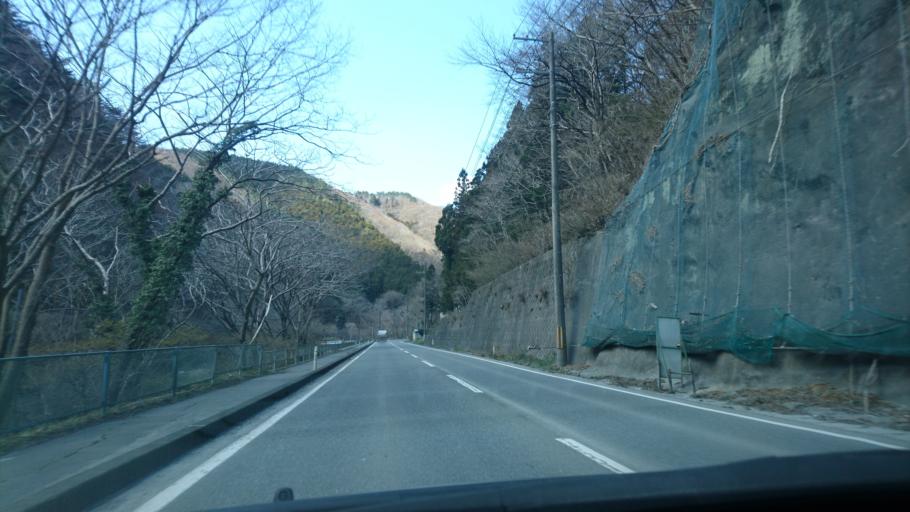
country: JP
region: Iwate
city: Ofunato
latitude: 39.1350
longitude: 141.6635
